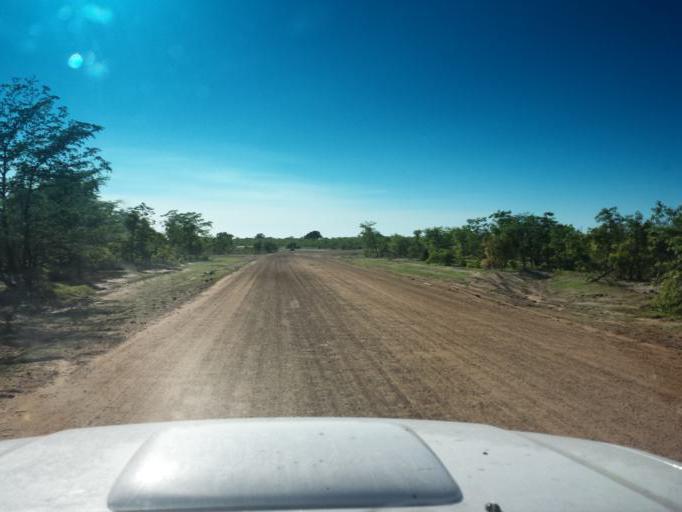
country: BW
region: North West
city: Shakawe
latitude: -18.2461
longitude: 21.7492
